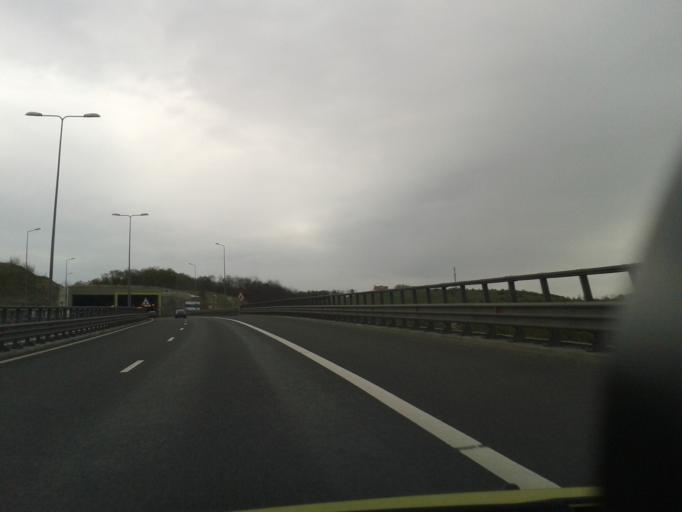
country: RO
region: Sibiu
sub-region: Comuna Orlat
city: Orlat
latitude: 45.7801
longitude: 23.9536
